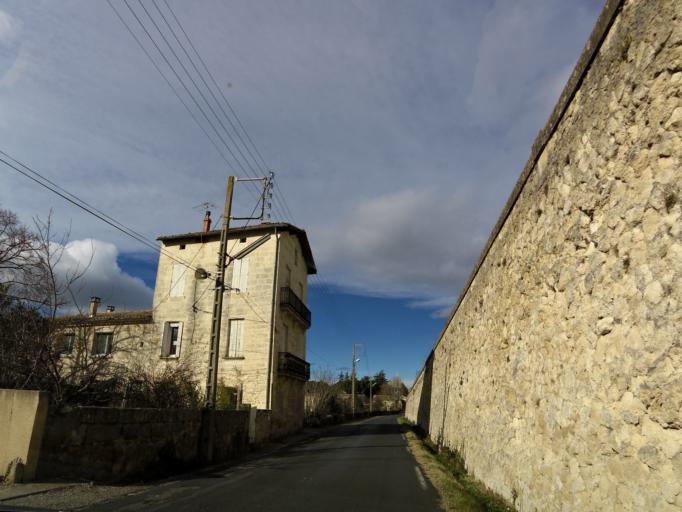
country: FR
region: Languedoc-Roussillon
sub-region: Departement du Gard
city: Sommieres
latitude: 43.7782
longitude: 4.0925
